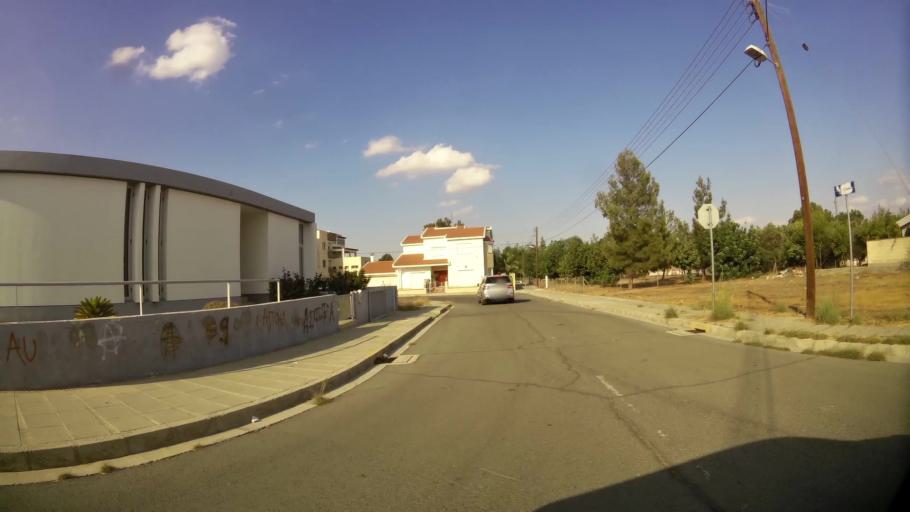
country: CY
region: Lefkosia
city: Kato Deftera
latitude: 35.1097
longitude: 33.2940
